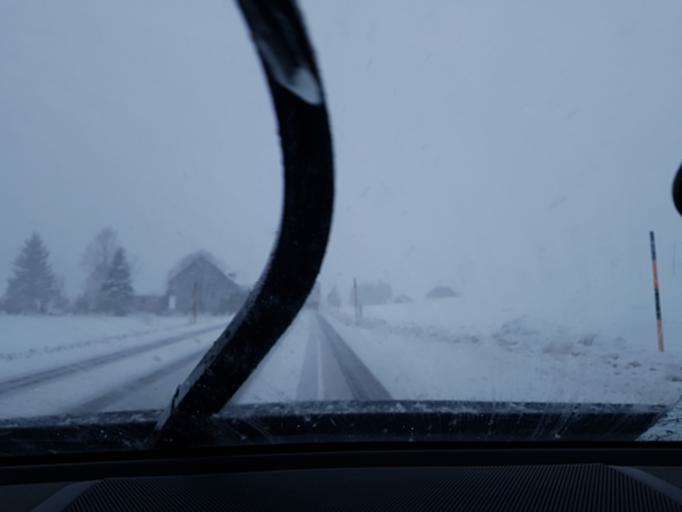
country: AT
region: Salzburg
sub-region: Politischer Bezirk Hallein
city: Abtenau
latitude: 47.5749
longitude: 13.3288
